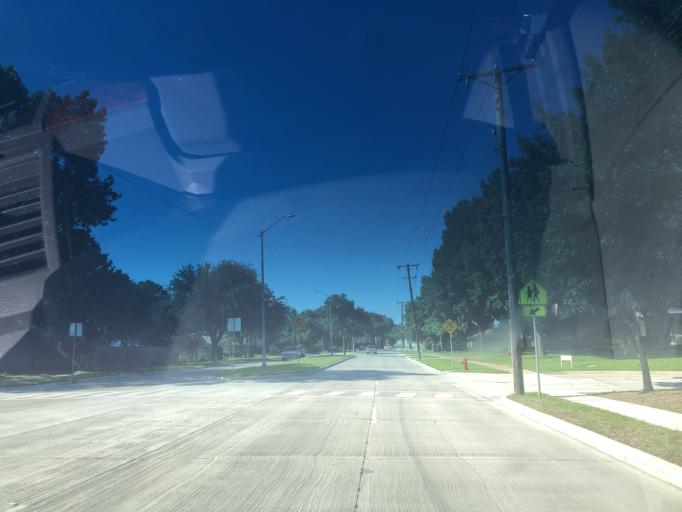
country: US
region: Texas
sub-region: Dallas County
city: Grand Prairie
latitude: 32.7169
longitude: -97.0150
